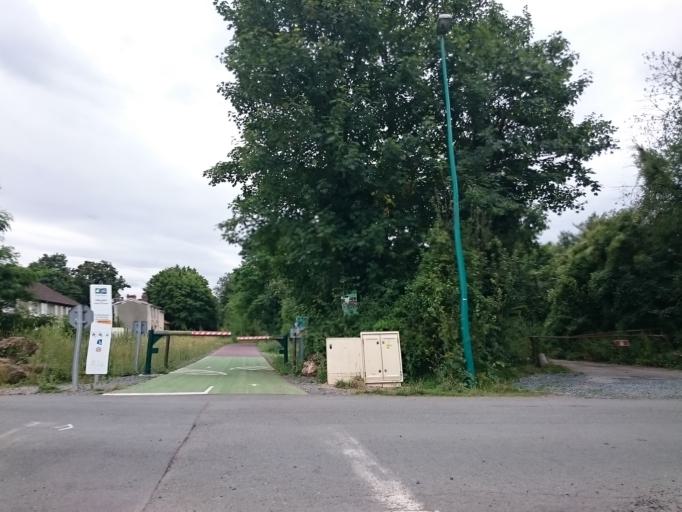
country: FR
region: Lower Normandy
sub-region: Departement du Calvados
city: Saint-Andre-sur-Orne
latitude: 49.1150
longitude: -0.3897
